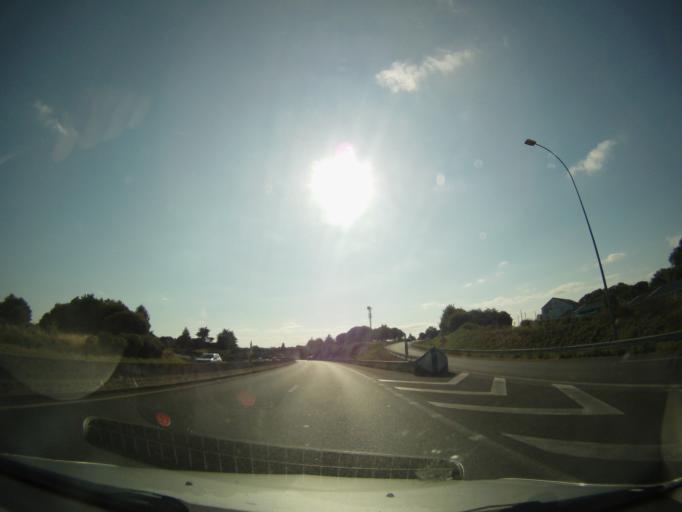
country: FR
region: Pays de la Loire
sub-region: Departement de la Loire-Atlantique
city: La Chapelle-sur-Erdre
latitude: 47.2757
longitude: -1.5449
